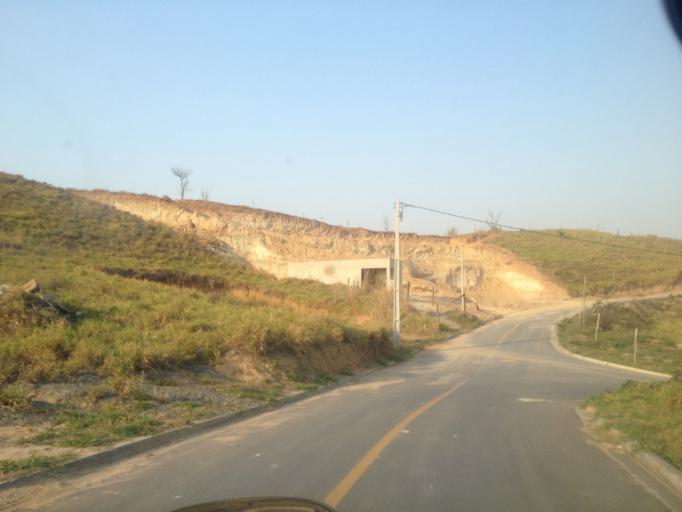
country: BR
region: Rio de Janeiro
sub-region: Porto Real
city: Porto Real
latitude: -22.4353
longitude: -44.3199
